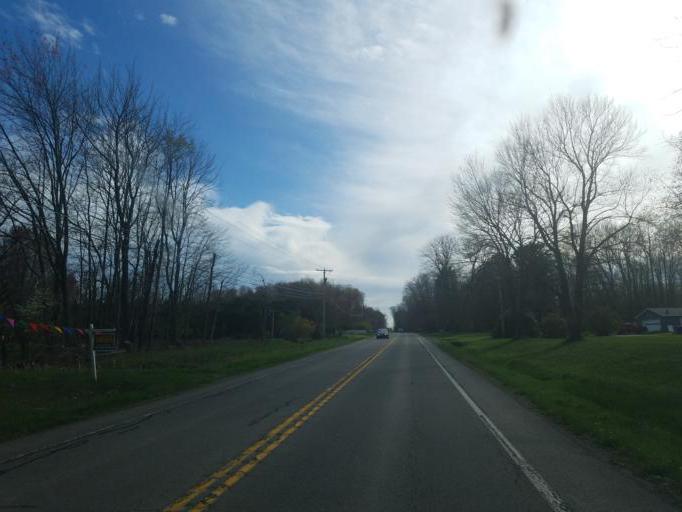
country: US
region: Pennsylvania
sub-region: Mercer County
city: Stoneboro
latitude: 41.3253
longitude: -80.1127
